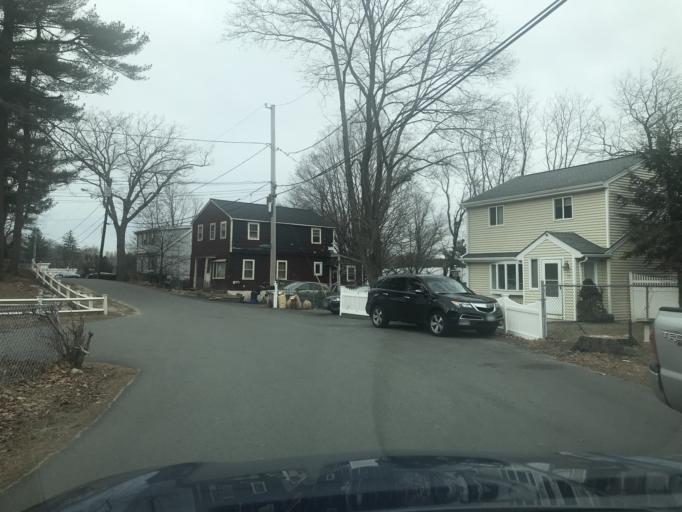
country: US
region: Massachusetts
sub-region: Essex County
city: Saugus
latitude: 42.4930
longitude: -71.0138
